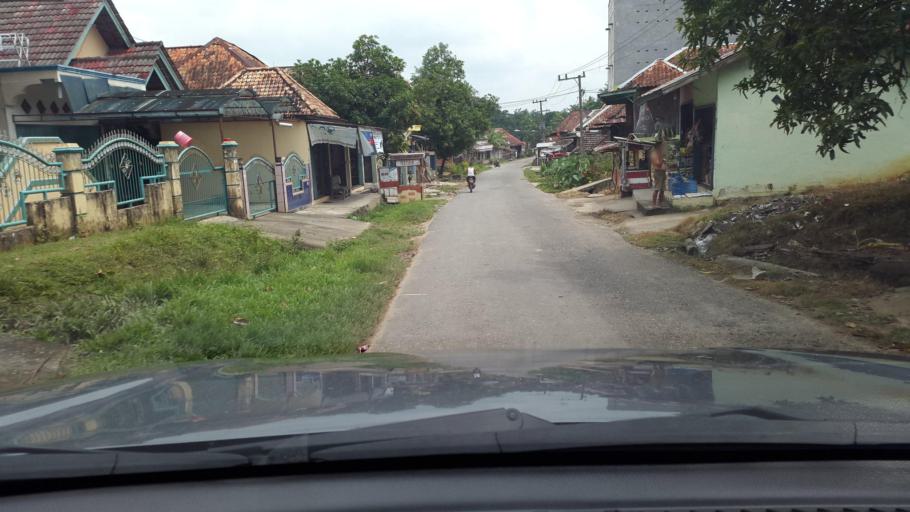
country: ID
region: South Sumatra
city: Gunungmenang
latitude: -3.0993
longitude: 103.8318
